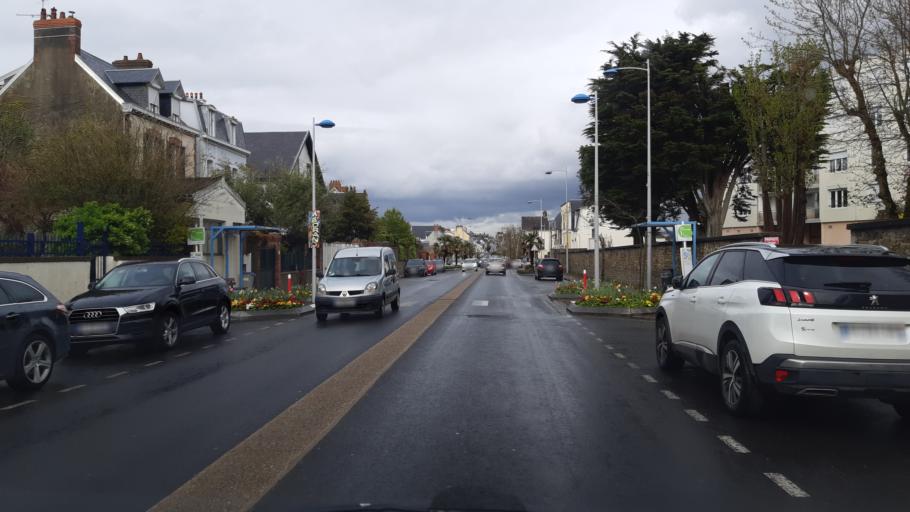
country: FR
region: Lower Normandy
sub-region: Departement de la Manche
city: Donville-les-Bains
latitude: 48.8444
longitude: -1.5854
